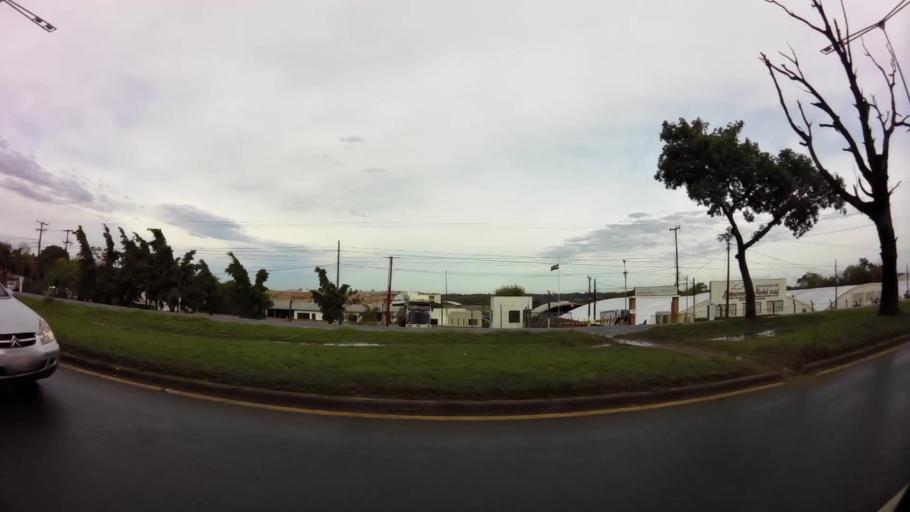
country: PY
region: Central
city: Fernando de la Mora
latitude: -25.2531
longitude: -57.5133
